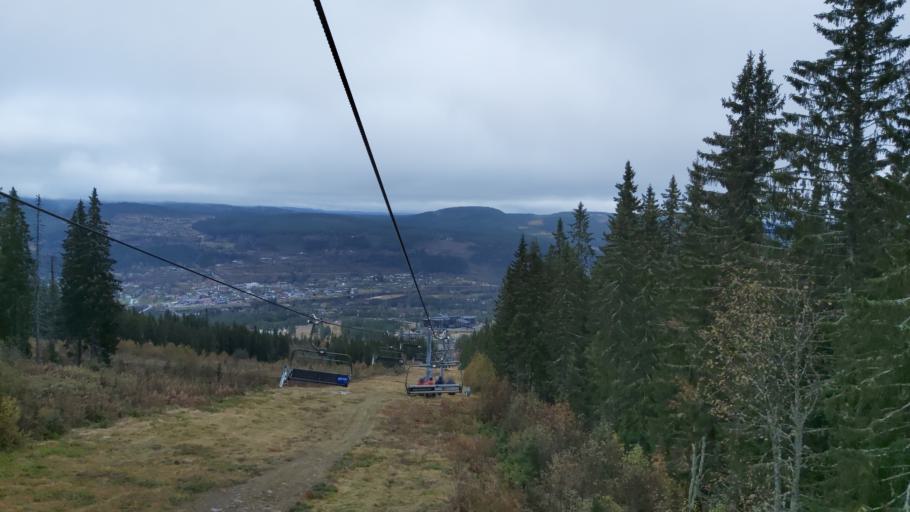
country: NO
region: Hedmark
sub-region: Trysil
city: Innbygda
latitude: 61.3083
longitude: 12.2176
